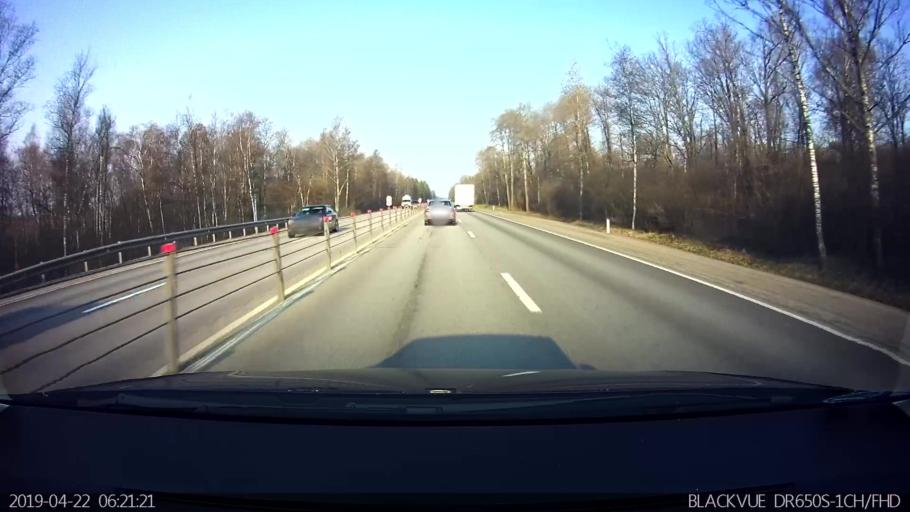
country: RU
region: Moskovskaya
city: Mozhaysk
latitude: 55.4650
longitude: 35.8764
